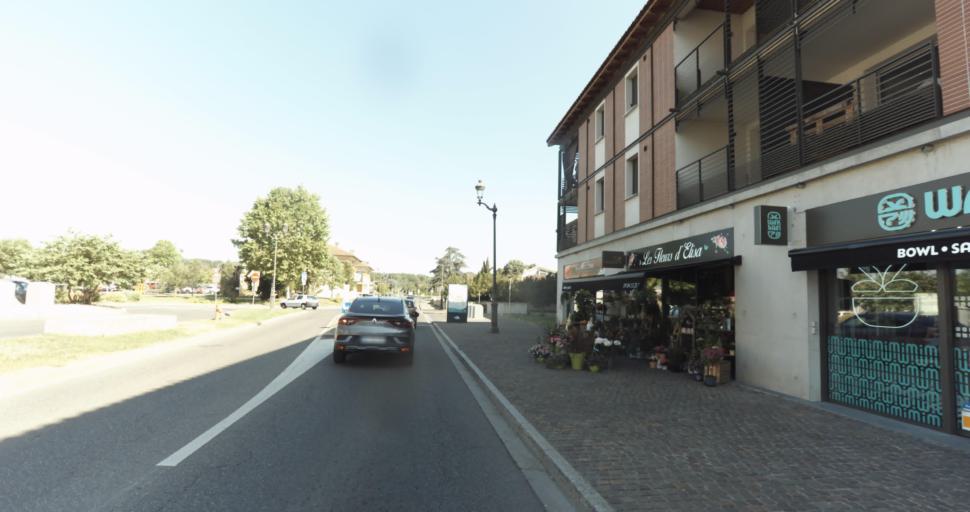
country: FR
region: Midi-Pyrenees
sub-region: Departement de la Haute-Garonne
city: Plaisance-du-Touch
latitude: 43.5670
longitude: 1.2972
